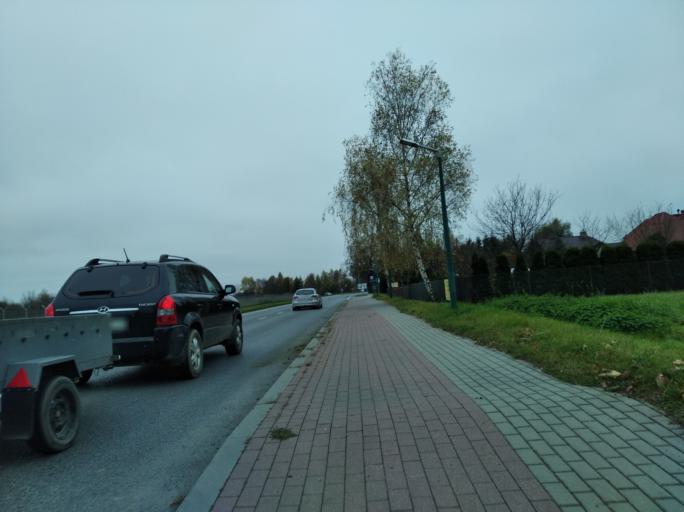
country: PL
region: Subcarpathian Voivodeship
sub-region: Krosno
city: Krosno
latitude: 49.6838
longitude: 21.7233
